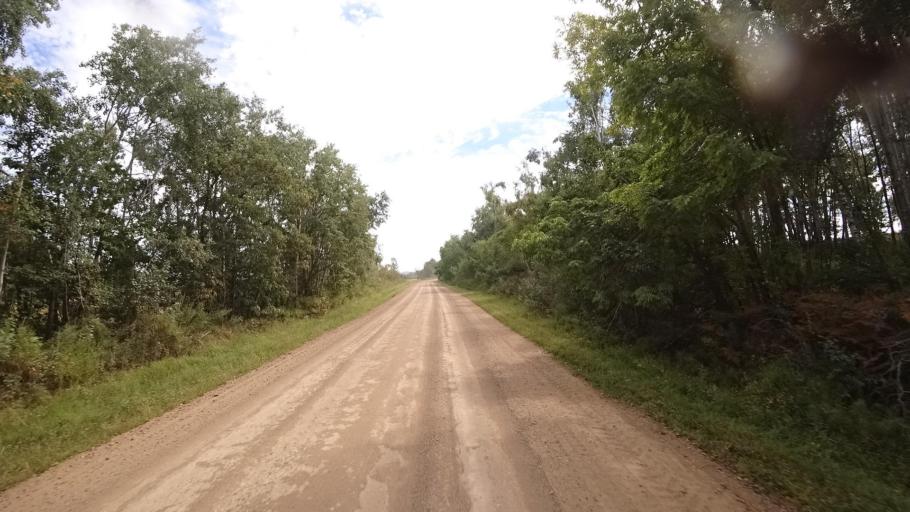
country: RU
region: Primorskiy
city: Yakovlevka
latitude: 44.5213
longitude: 133.5952
